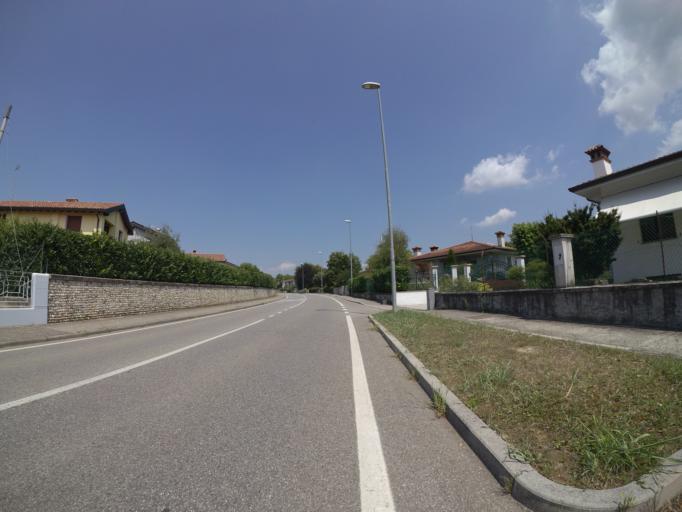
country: IT
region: Friuli Venezia Giulia
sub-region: Provincia di Udine
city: Codroipo
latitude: 45.9787
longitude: 12.9728
